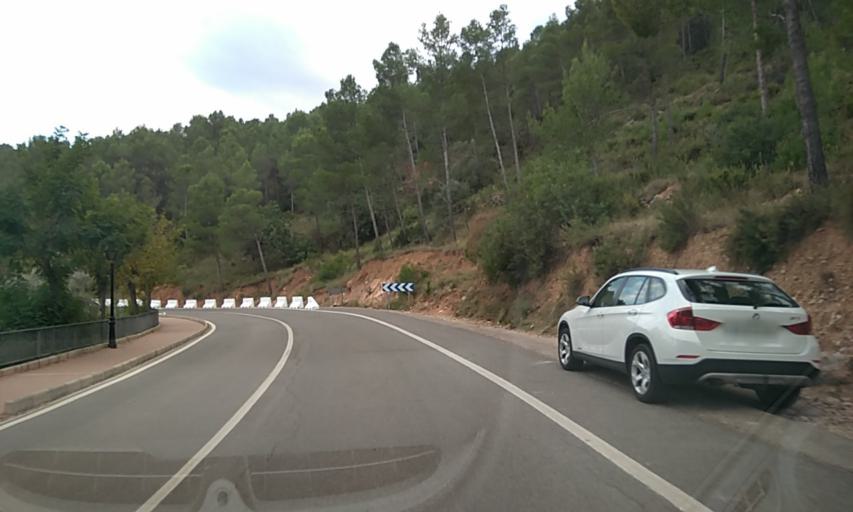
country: ES
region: Valencia
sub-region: Provincia de Castello
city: Montanejos
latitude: 40.0743
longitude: -0.5299
